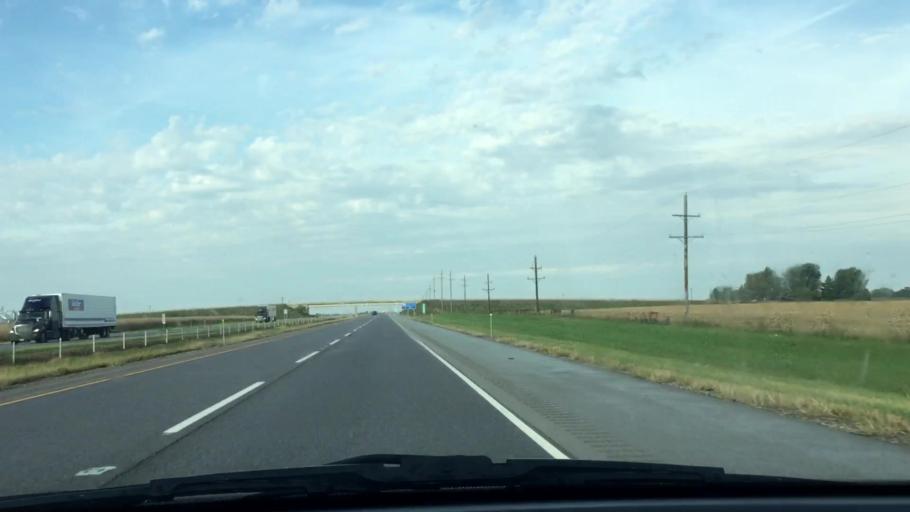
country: US
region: Illinois
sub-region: Lee County
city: Franklin Grove
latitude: 41.8230
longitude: -89.3841
